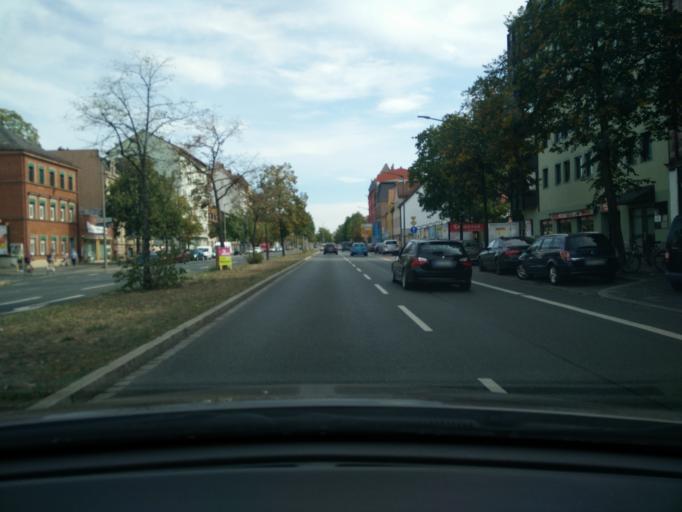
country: DE
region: Bavaria
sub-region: Regierungsbezirk Mittelfranken
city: Wetzendorf
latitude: 49.4568
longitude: 11.0376
